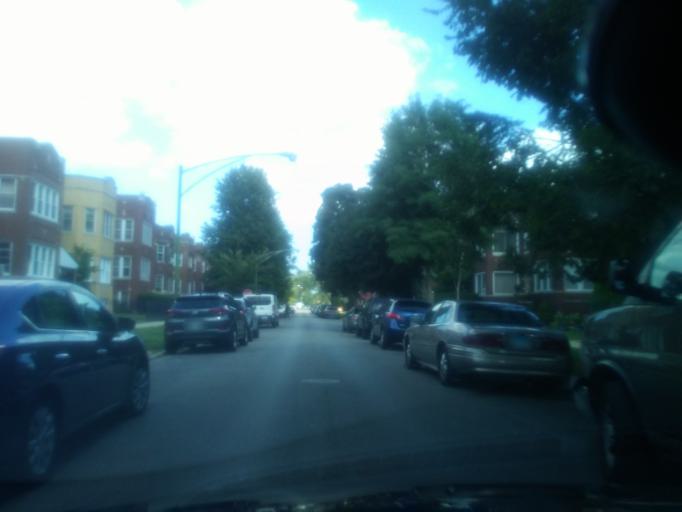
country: US
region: Illinois
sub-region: Cook County
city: Lincolnwood
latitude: 41.9588
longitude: -87.7555
